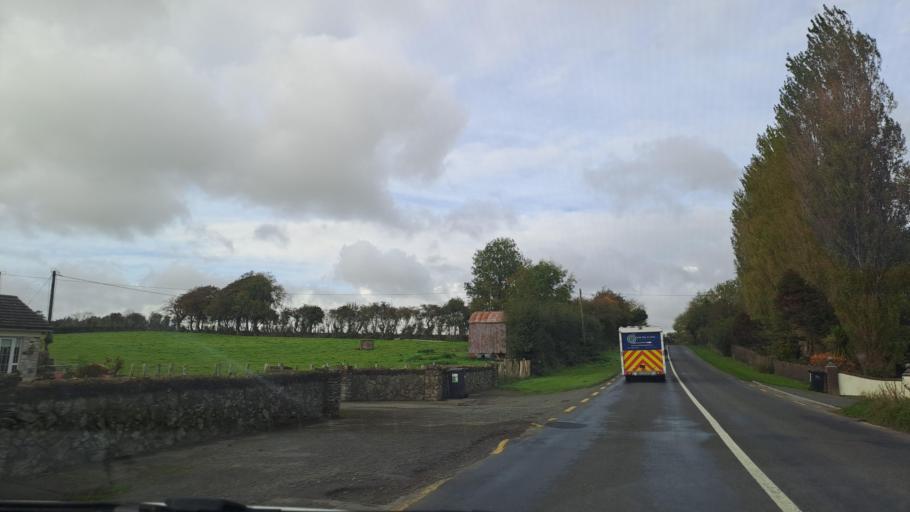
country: IE
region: Ulster
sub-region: An Cabhan
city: Kingscourt
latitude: 53.8040
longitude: -6.7367
